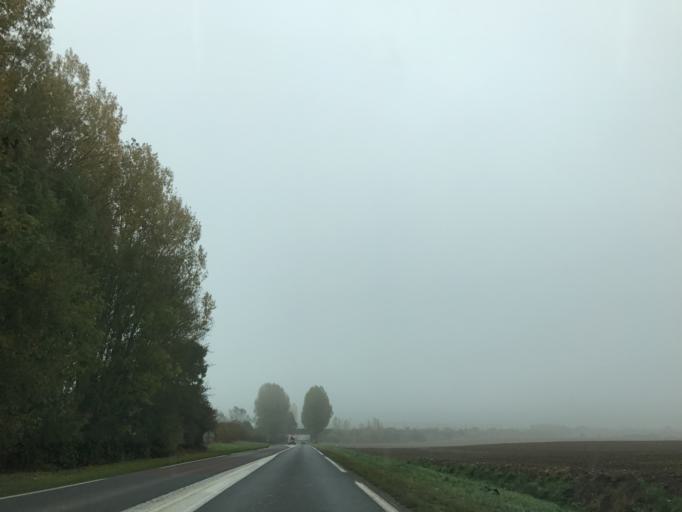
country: FR
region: Nord-Pas-de-Calais
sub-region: Departement du Pas-de-Calais
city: Bapaume
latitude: 50.0914
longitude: 2.8663
